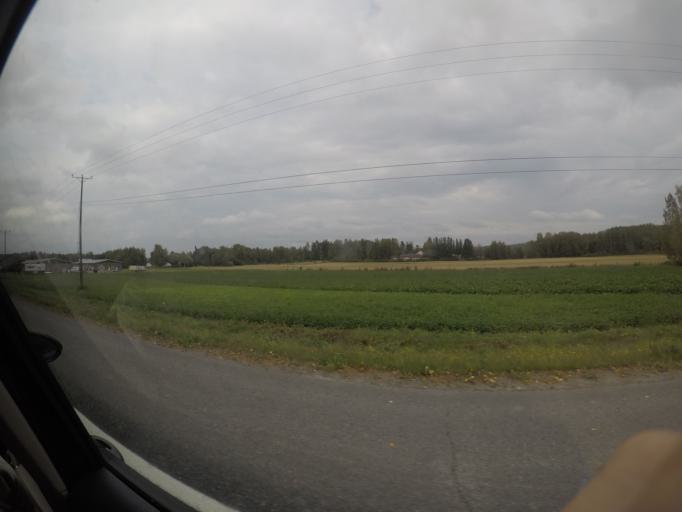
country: FI
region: Haeme
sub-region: Haemeenlinna
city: Parola
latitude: 61.0345
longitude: 24.4115
